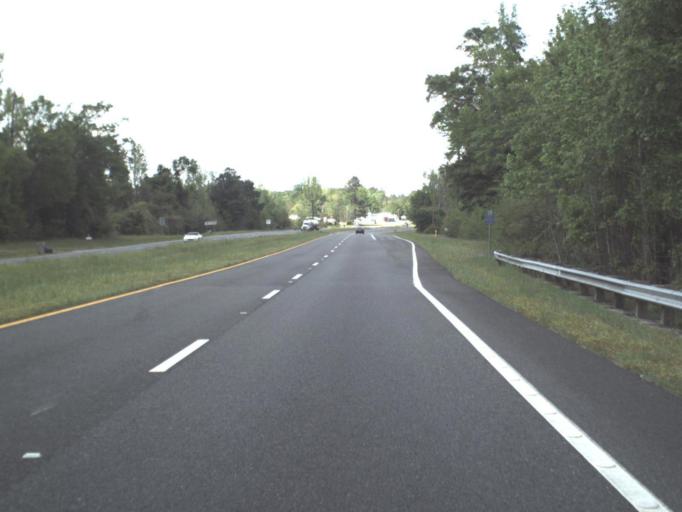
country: US
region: Florida
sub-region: Escambia County
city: Century
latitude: 30.8647
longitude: -87.3234
